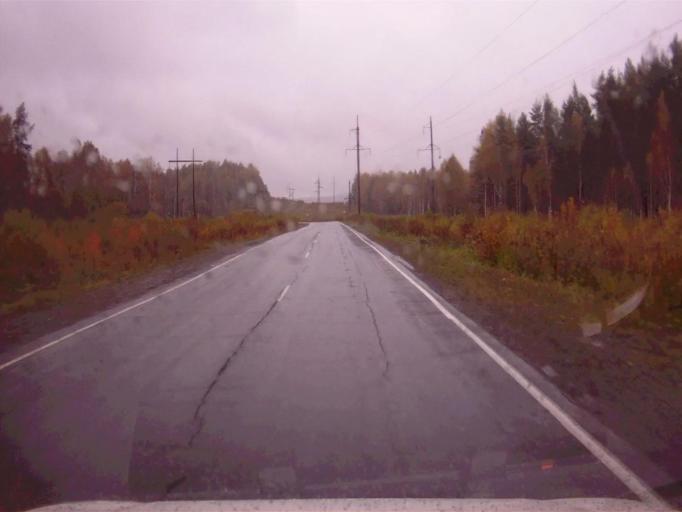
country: RU
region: Chelyabinsk
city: Verkhniy Ufaley
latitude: 55.9482
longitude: 60.4033
